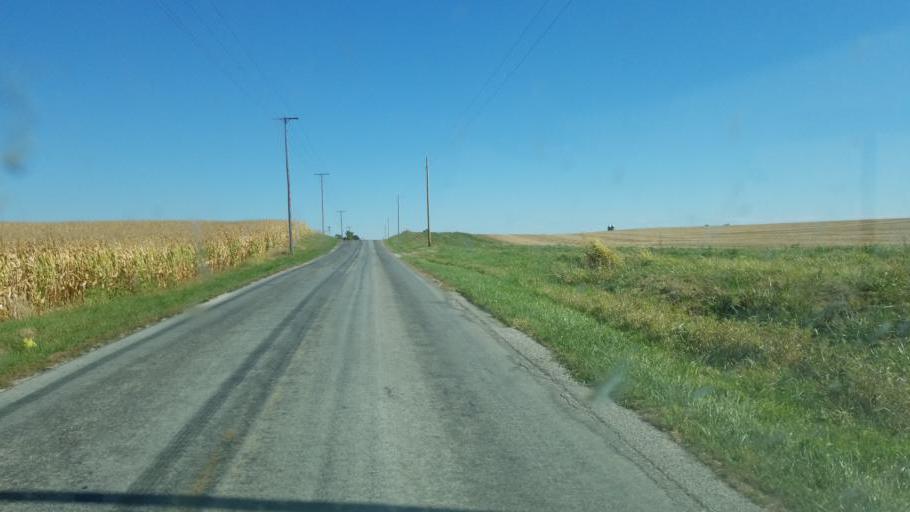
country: US
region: Ohio
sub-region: Huron County
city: Greenwich
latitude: 40.9941
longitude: -82.5793
